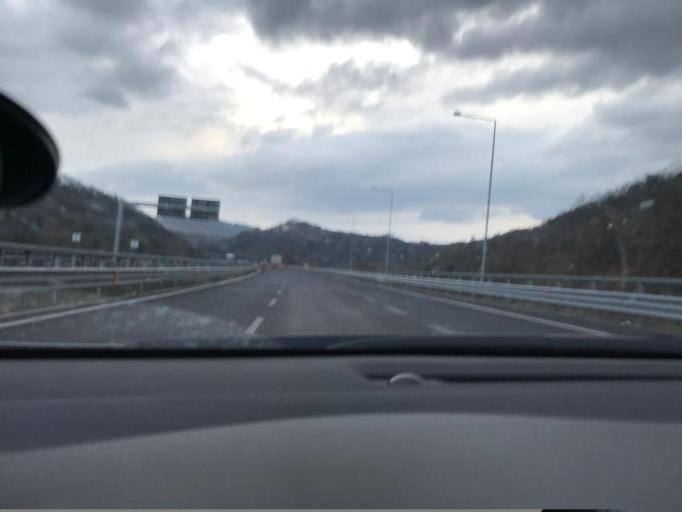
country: IT
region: Umbria
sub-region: Provincia di Perugia
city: Valfabbrica
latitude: 43.1554
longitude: 12.5863
